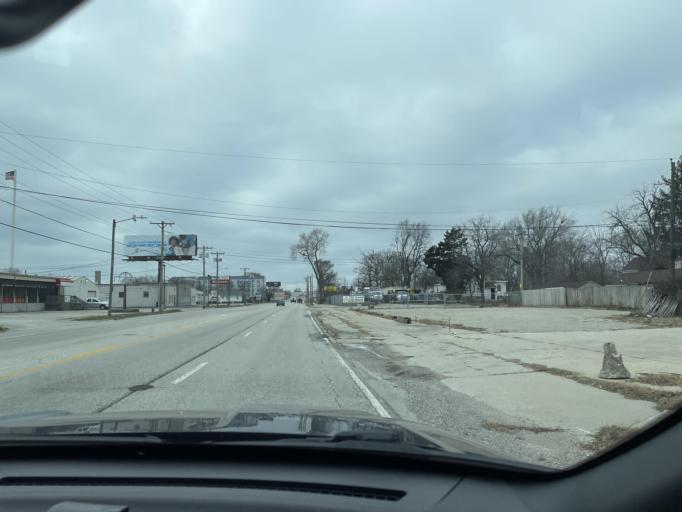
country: US
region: Illinois
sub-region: Sangamon County
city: Grandview
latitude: 39.8020
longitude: -89.6218
